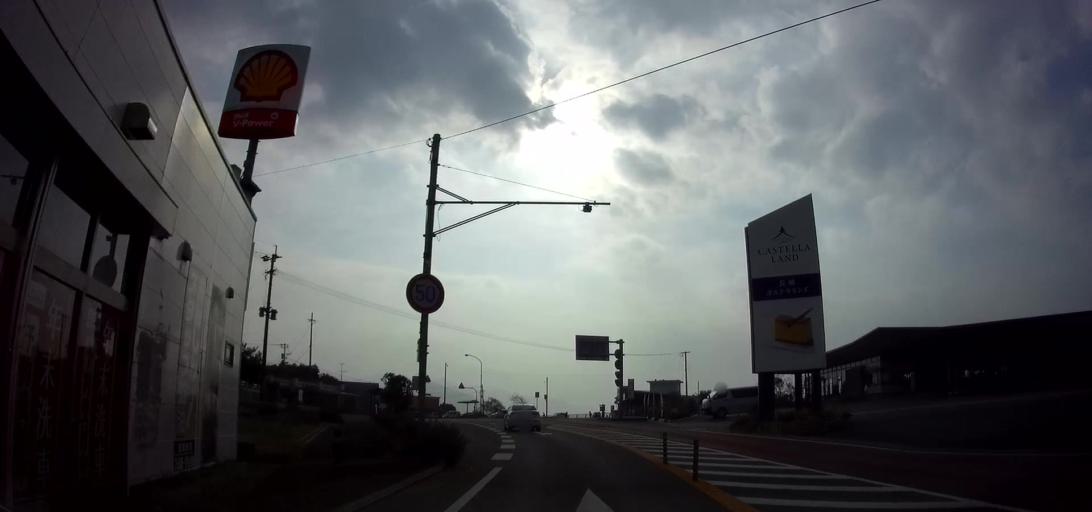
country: JP
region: Nagasaki
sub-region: Isahaya-shi
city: Isahaya
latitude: 32.7959
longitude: 130.1655
